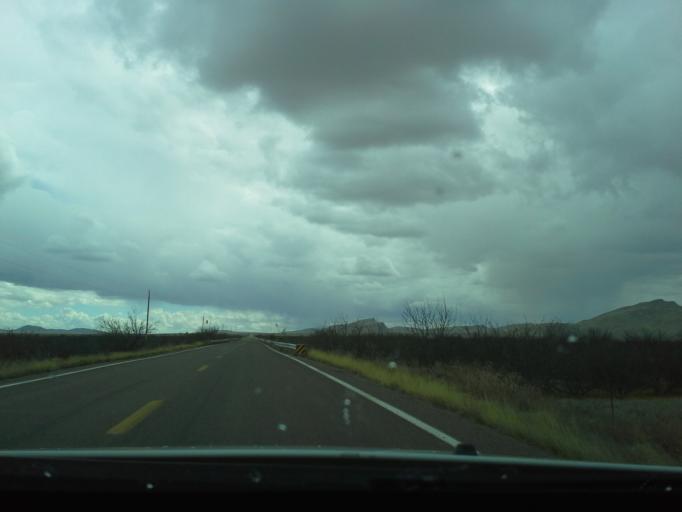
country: US
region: Arizona
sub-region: Cochise County
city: Douglas
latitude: 31.7412
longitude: -109.0976
